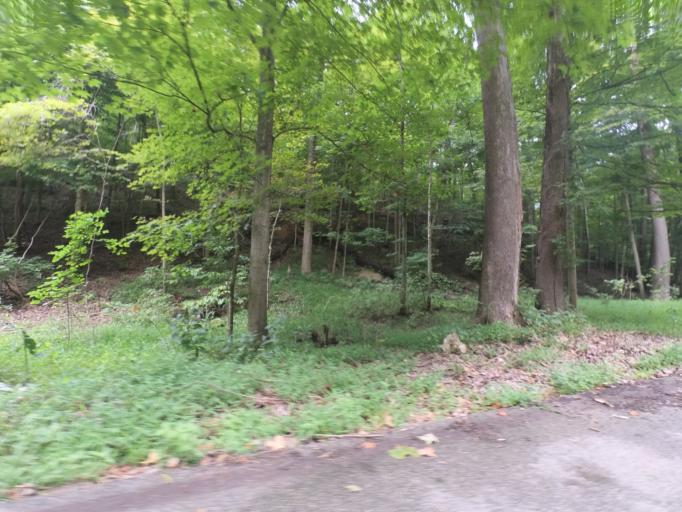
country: US
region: West Virginia
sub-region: Cabell County
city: Huntington
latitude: 38.3862
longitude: -82.4339
